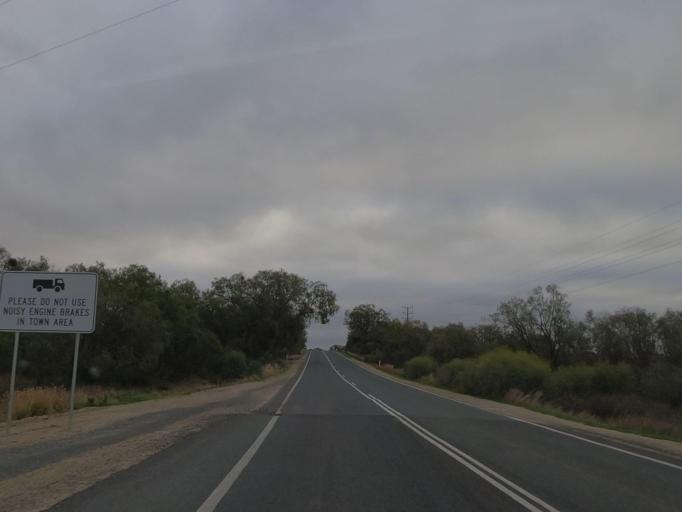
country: AU
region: Victoria
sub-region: Swan Hill
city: Swan Hill
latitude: -35.4691
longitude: 143.6615
